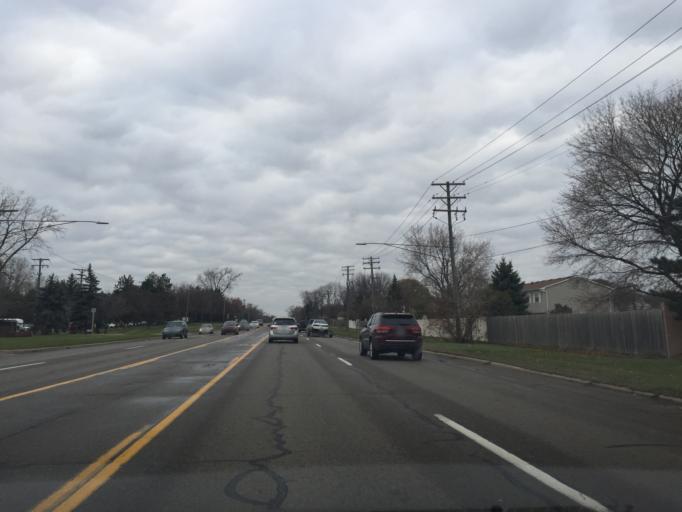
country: US
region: Michigan
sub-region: Wayne County
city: Livonia
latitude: 42.3858
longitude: -83.3338
